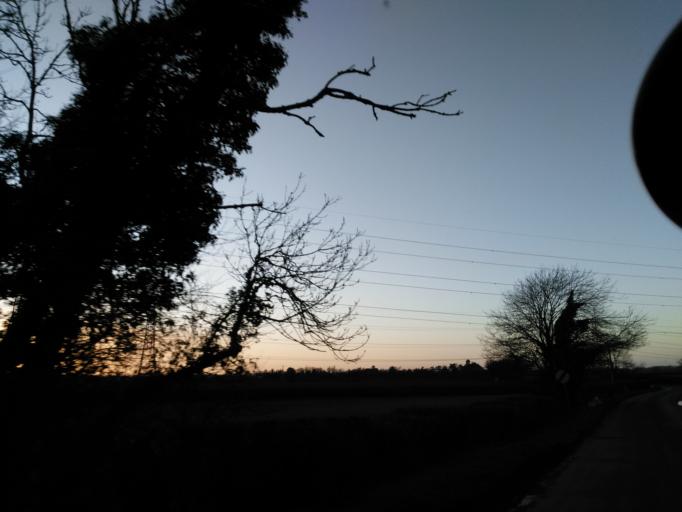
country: GB
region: England
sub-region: Wiltshire
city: Lacock
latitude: 51.4243
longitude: -2.1411
